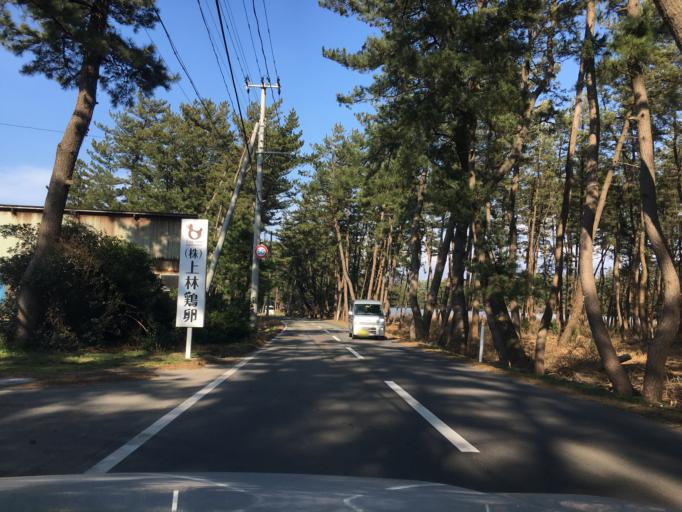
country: JP
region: Yamagata
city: Tsuruoka
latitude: 38.8063
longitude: 139.7768
